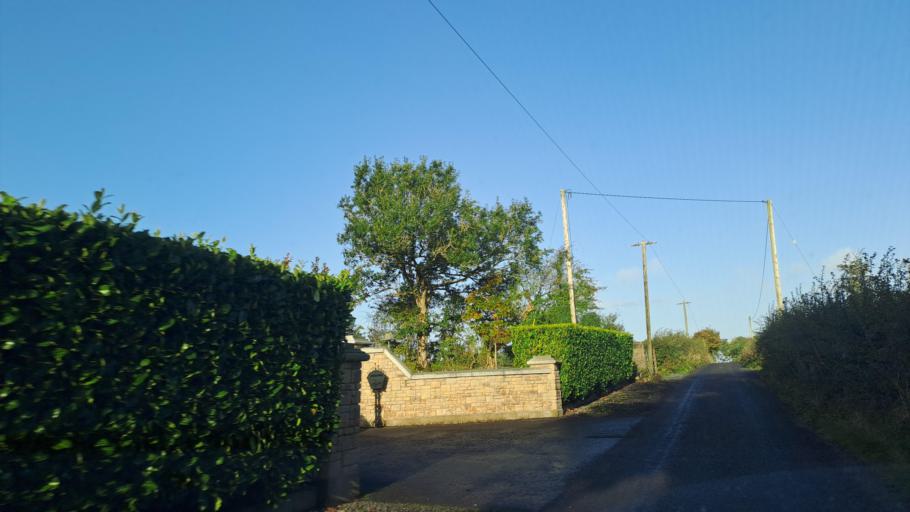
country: IE
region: Ulster
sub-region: County Monaghan
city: Castleblayney
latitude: 54.0912
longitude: -6.8723
